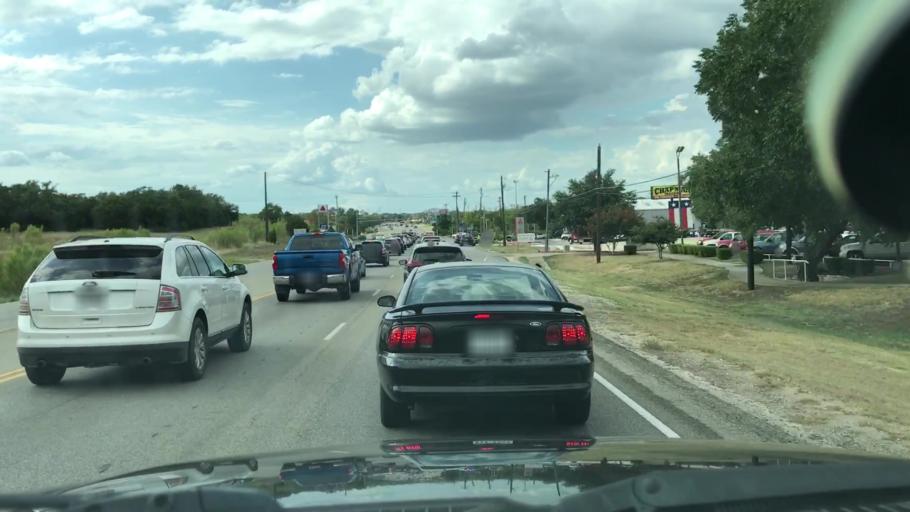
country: US
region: Texas
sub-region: Williamson County
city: Cedar Park
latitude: 30.4984
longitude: -97.8165
